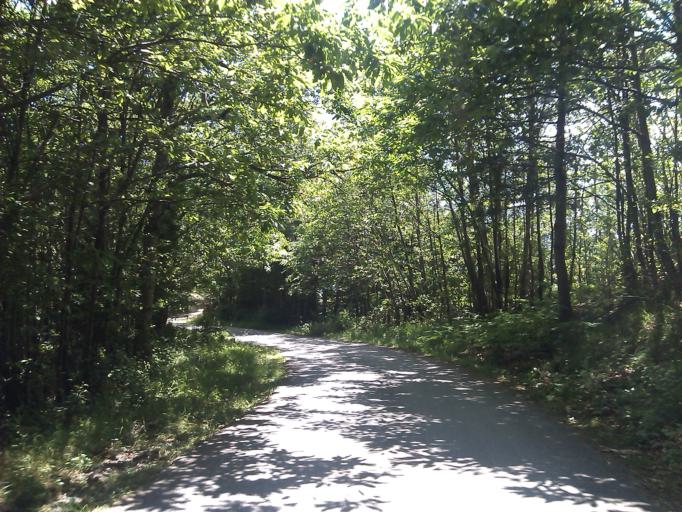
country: IT
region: Tuscany
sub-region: Provincia di Prato
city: Cantagallo
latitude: 43.9885
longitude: 11.0397
